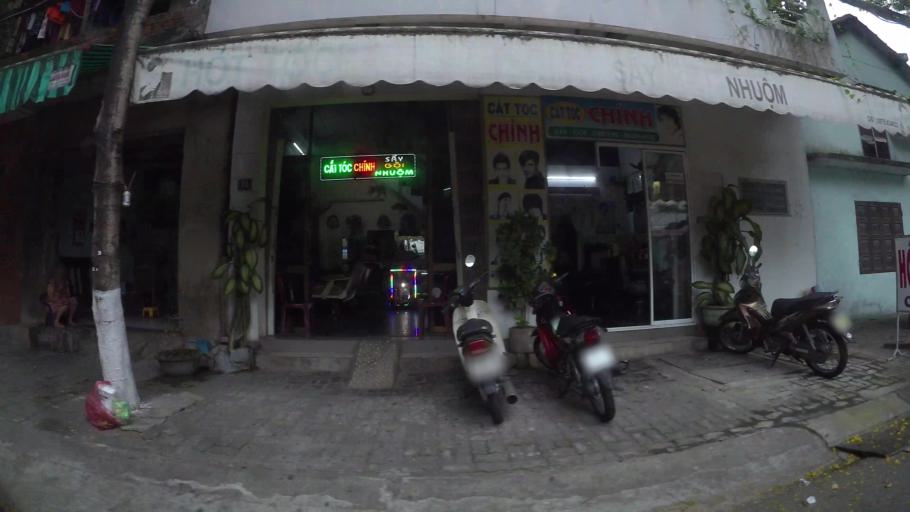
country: VN
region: Da Nang
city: Da Nang
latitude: 16.0745
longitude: 108.2102
